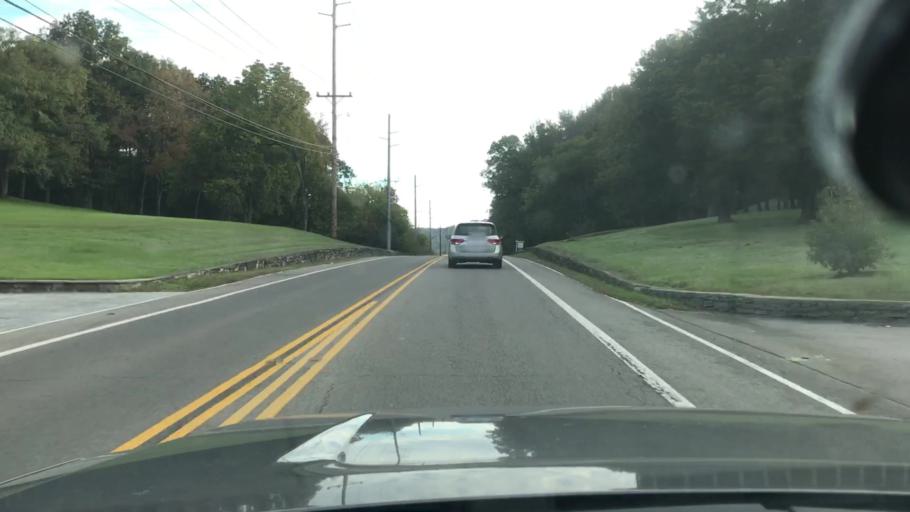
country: US
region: Tennessee
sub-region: Davidson County
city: Forest Hills
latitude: 36.0650
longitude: -86.8469
